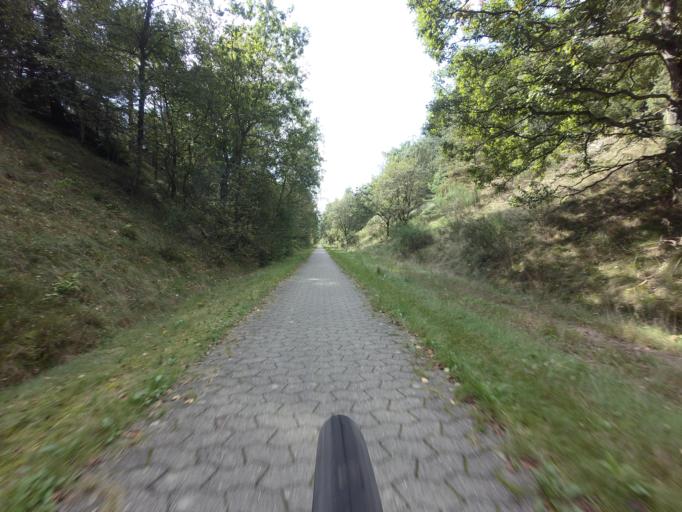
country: DK
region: Central Jutland
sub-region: Viborg Kommune
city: Viborg
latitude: 56.3841
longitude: 9.2944
